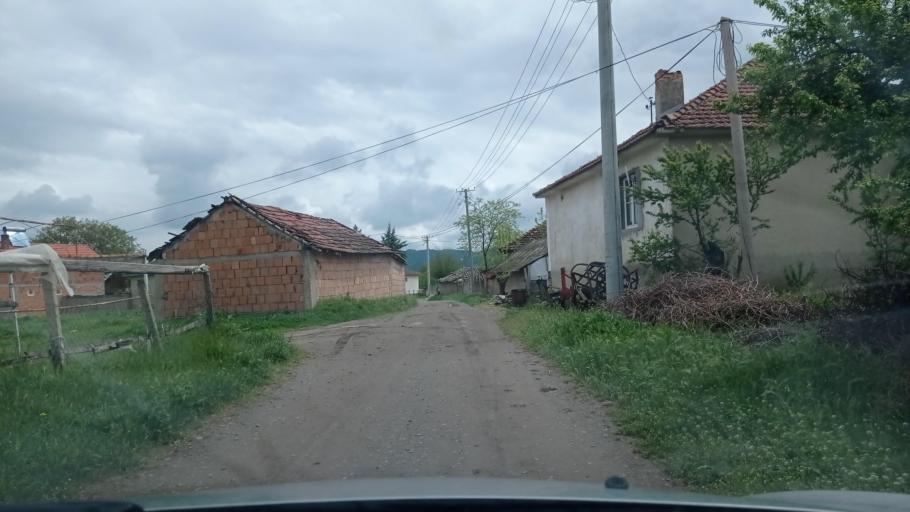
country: MK
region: Lozovo
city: Lozovo
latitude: 41.7662
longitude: 21.8947
